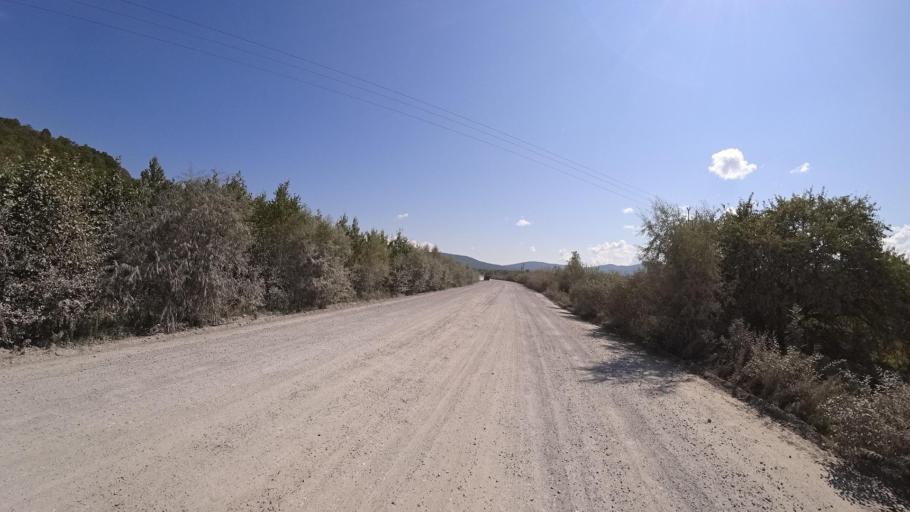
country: RU
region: Jewish Autonomous Oblast
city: Londoko
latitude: 49.0038
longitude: 131.9221
